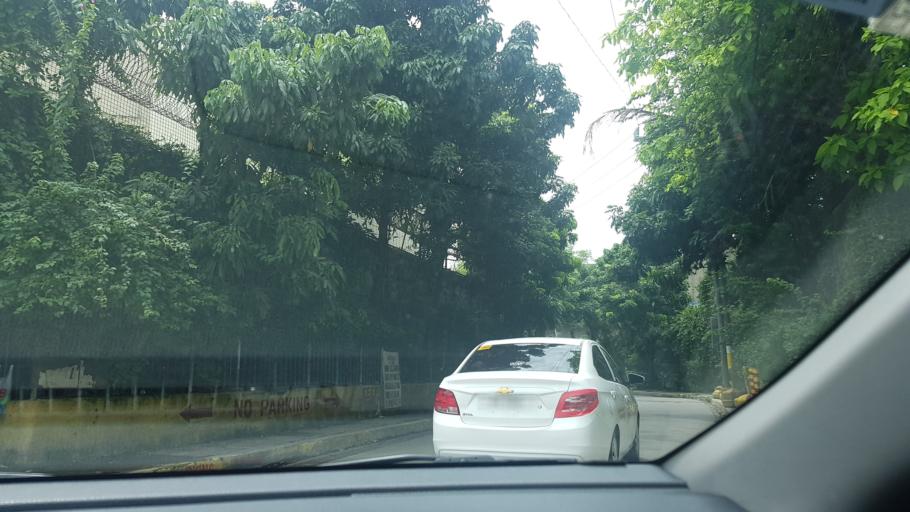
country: PH
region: Calabarzon
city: Del Monte
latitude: 14.6530
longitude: 121.0021
